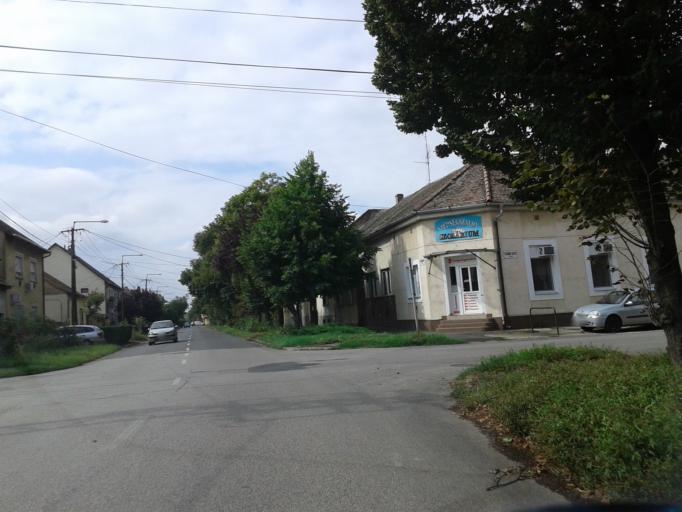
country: HU
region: Csongrad
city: Szeged
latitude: 46.2386
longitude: 20.1337
